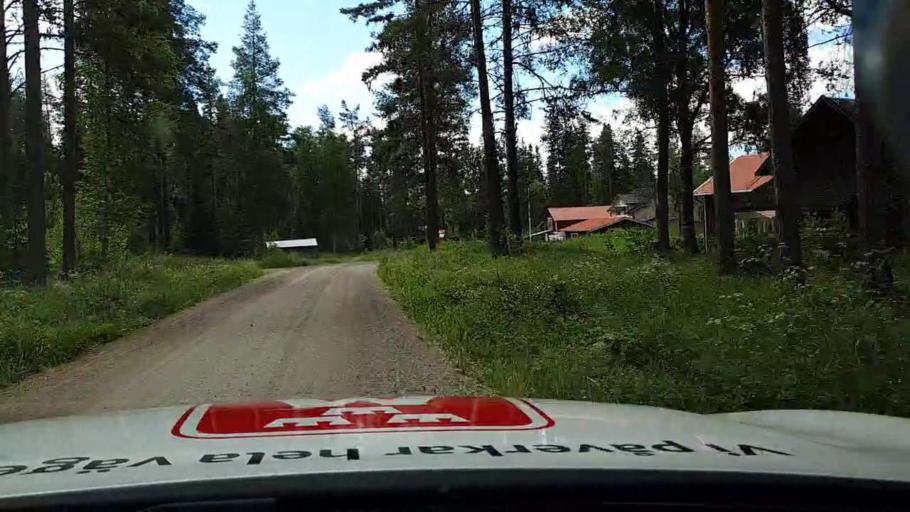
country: SE
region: Jaemtland
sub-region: Braecke Kommun
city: Braecke
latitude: 62.7532
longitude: 15.5033
